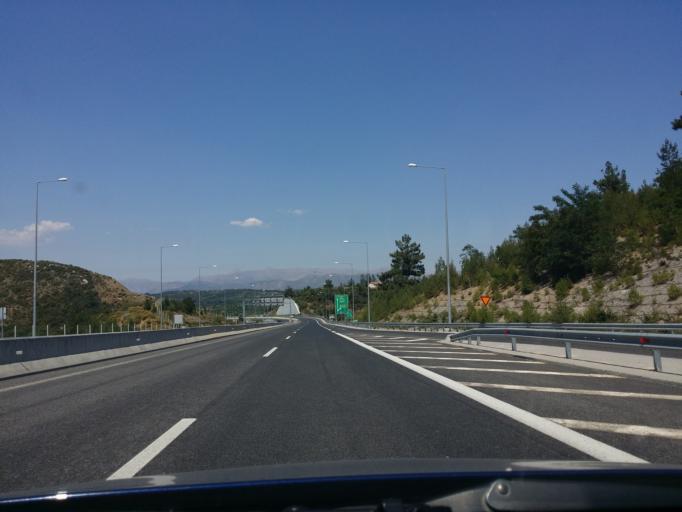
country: GR
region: Peloponnese
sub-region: Nomos Arkadias
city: Tripoli
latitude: 37.4506
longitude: 22.3243
